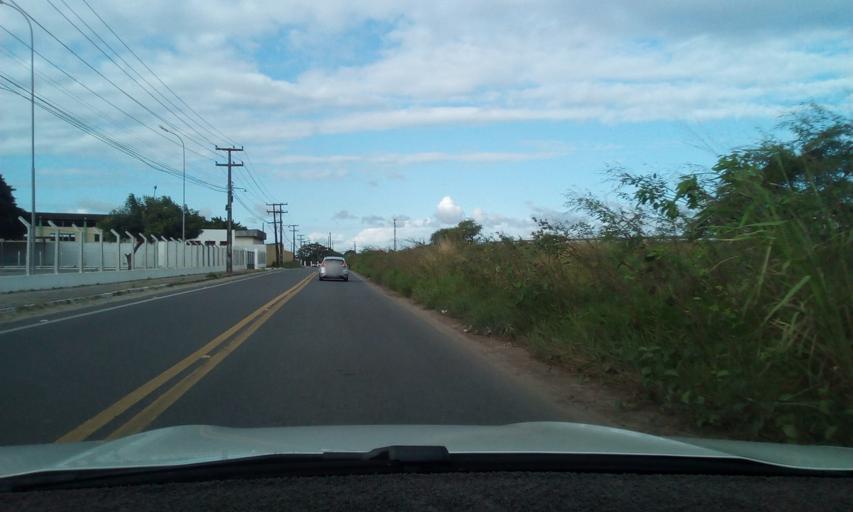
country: BR
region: Paraiba
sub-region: Santa Rita
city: Santa Rita
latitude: -7.1350
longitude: -34.9654
